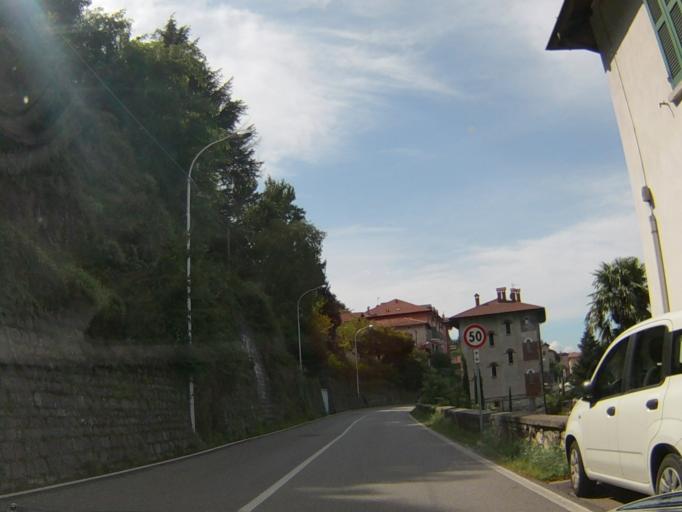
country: IT
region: Lombardy
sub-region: Provincia di Lecco
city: Bellano
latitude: 46.0514
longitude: 9.3108
